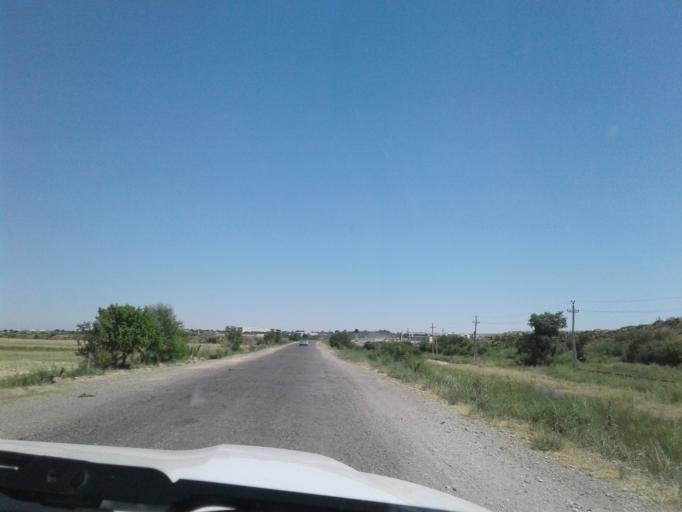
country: AF
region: Badghis
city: Bala Murghab
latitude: 35.9698
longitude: 62.9064
